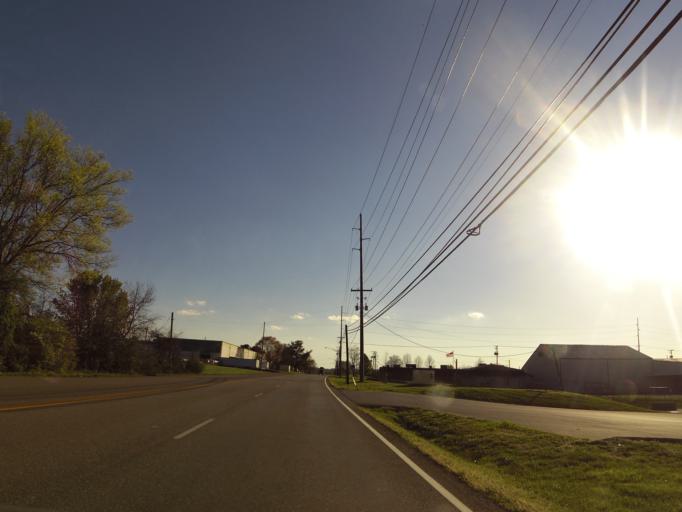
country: US
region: Tennessee
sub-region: Knox County
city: Knoxville
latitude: 35.9527
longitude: -83.8311
